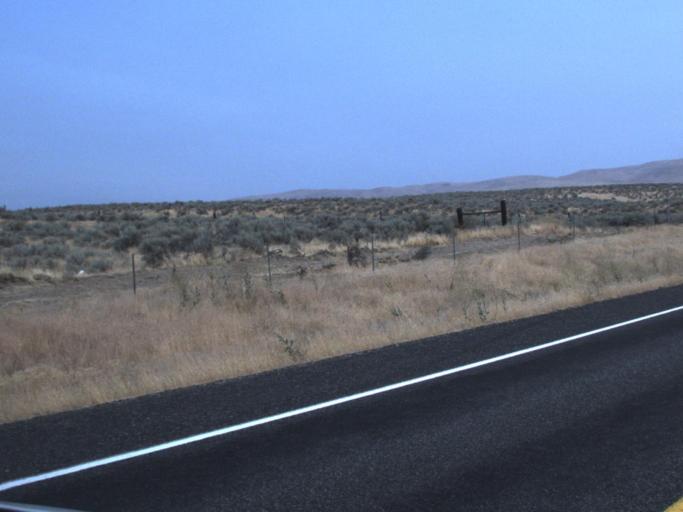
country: US
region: Washington
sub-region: Yakima County
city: Toppenish
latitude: 46.2466
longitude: -120.4178
